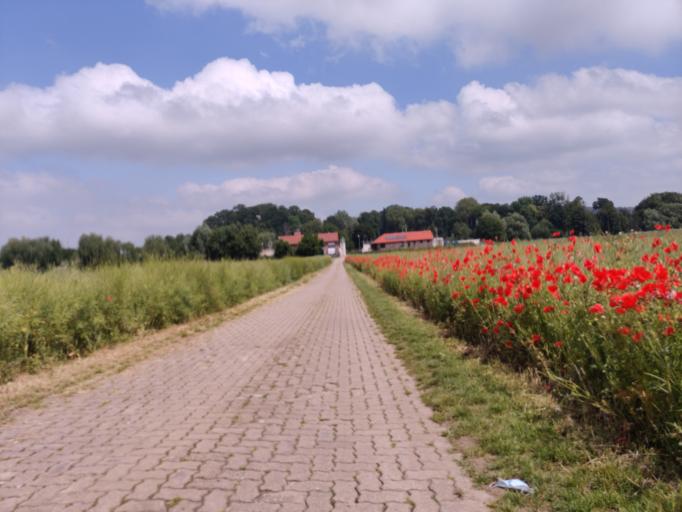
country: DE
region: Lower Saxony
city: Bad Salzdetfurth
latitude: 52.1012
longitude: 10.0104
